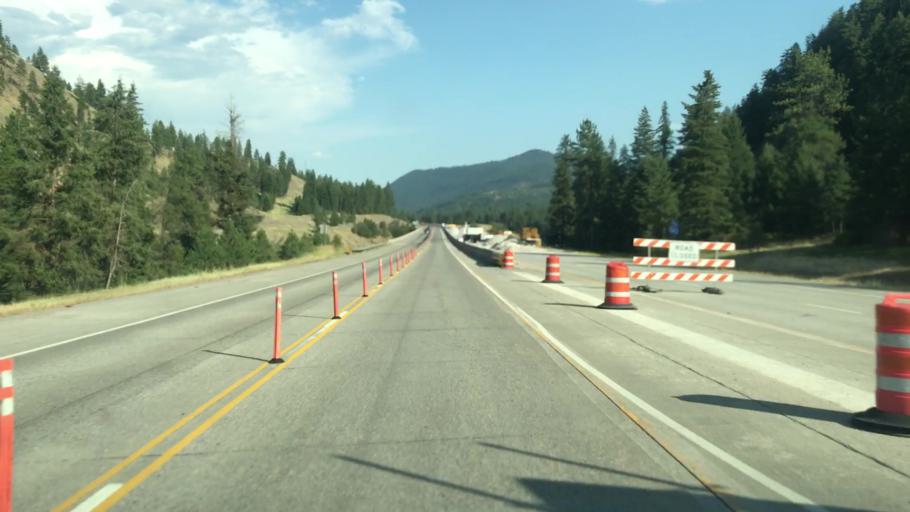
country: US
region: Montana
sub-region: Mineral County
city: Superior
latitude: 47.2229
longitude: -114.9644
